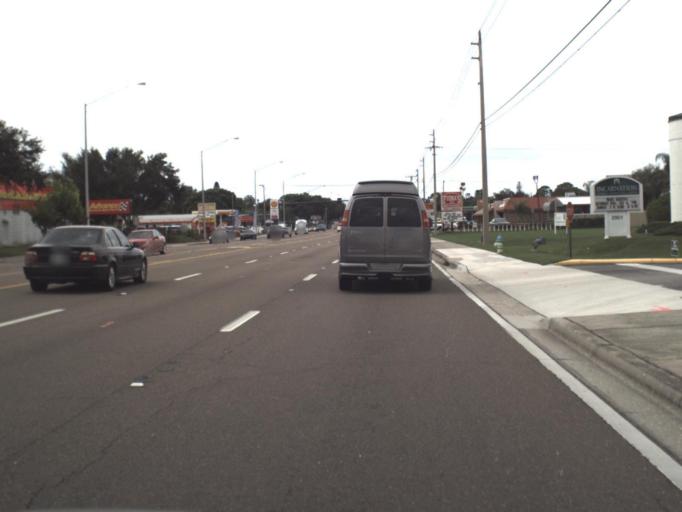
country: US
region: Florida
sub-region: Sarasota County
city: Southgate
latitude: 27.2989
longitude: -82.5117
